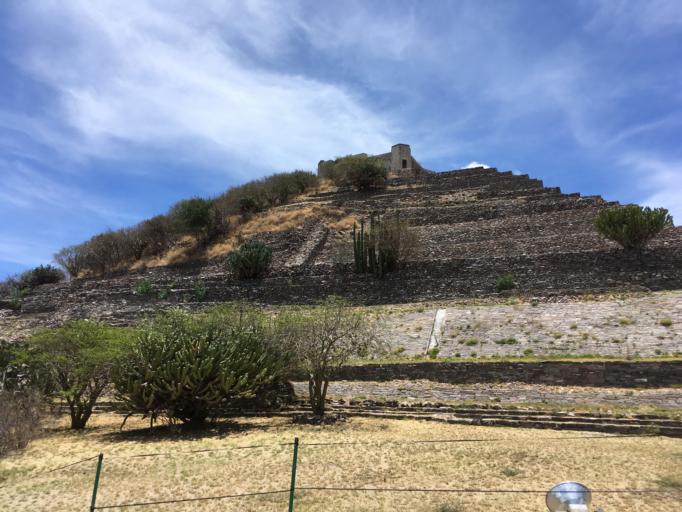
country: MX
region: Queretaro
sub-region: Corregidora
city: El Pueblito
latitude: 20.5506
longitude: -100.4438
